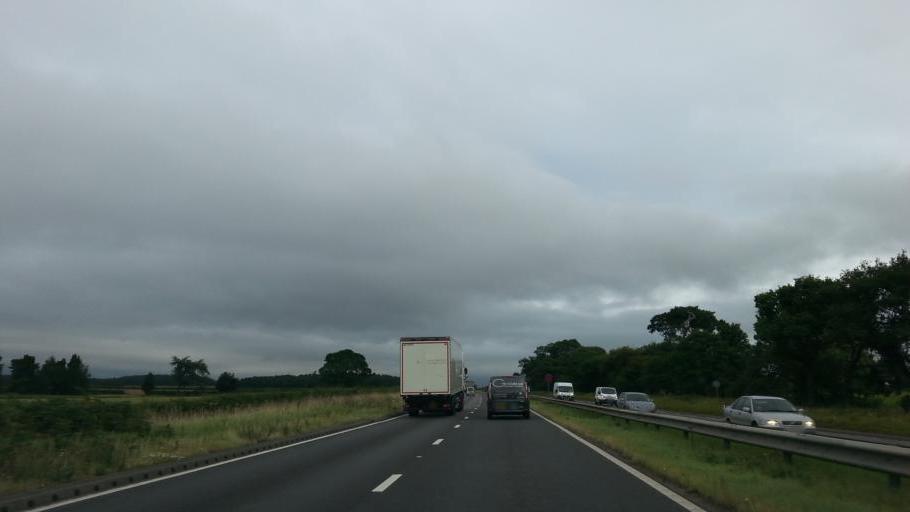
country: GB
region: England
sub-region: Nottinghamshire
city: Babworth
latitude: 53.3405
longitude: -1.0294
